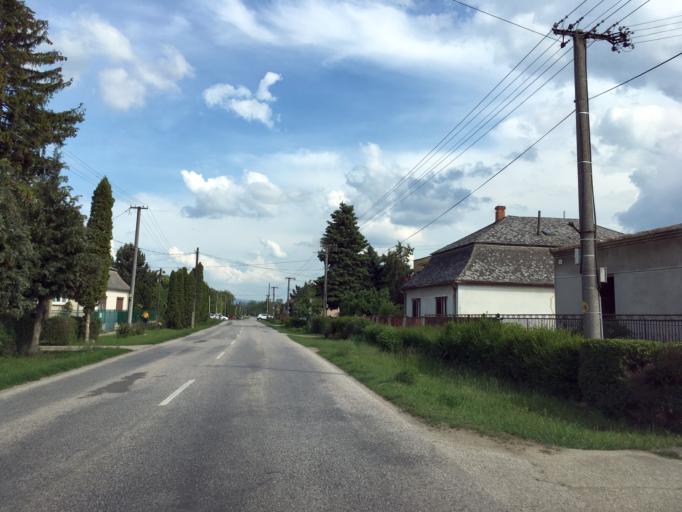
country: HU
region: Komarom-Esztergom
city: Almasfuzito
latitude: 47.8026
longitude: 18.2351
